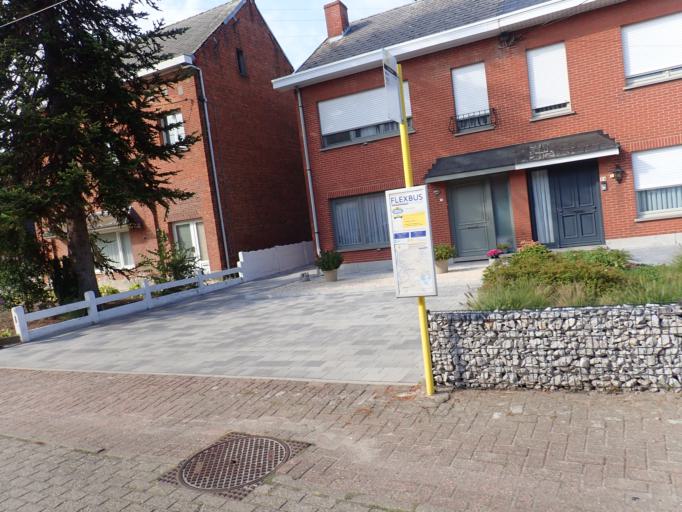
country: BE
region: Flanders
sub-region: Provincie Antwerpen
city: Bornem
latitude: 51.0703
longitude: 4.2405
